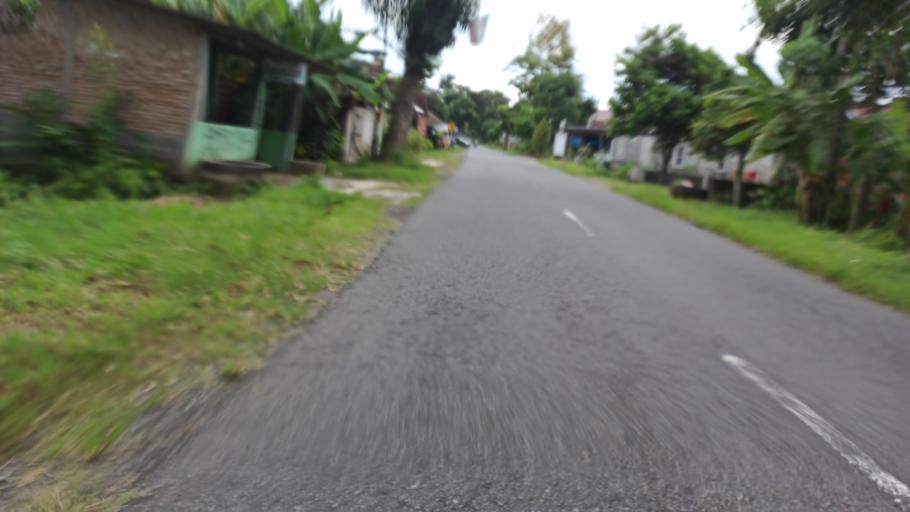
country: ID
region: Daerah Istimewa Yogyakarta
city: Sleman
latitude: -7.6966
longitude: 110.2917
